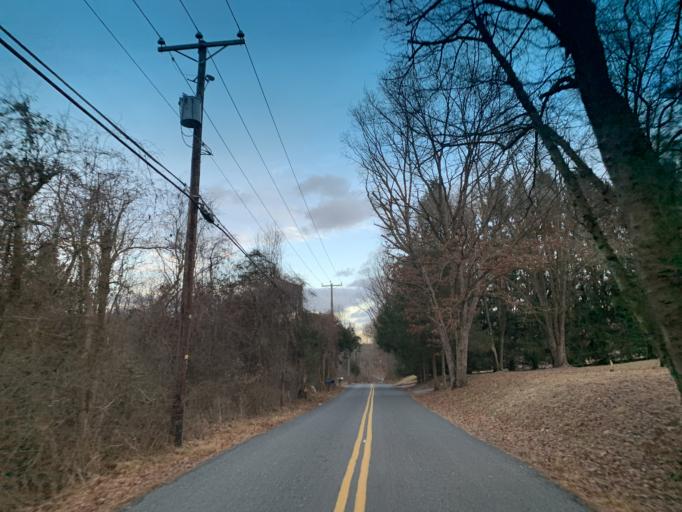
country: US
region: Pennsylvania
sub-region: York County
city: Susquehanna Trails
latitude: 39.6565
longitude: -76.3039
